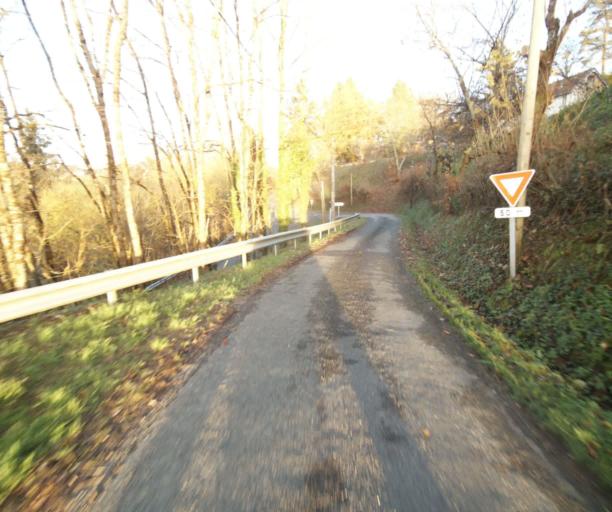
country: FR
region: Limousin
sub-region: Departement de la Correze
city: Laguenne
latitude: 45.2348
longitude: 1.8160
